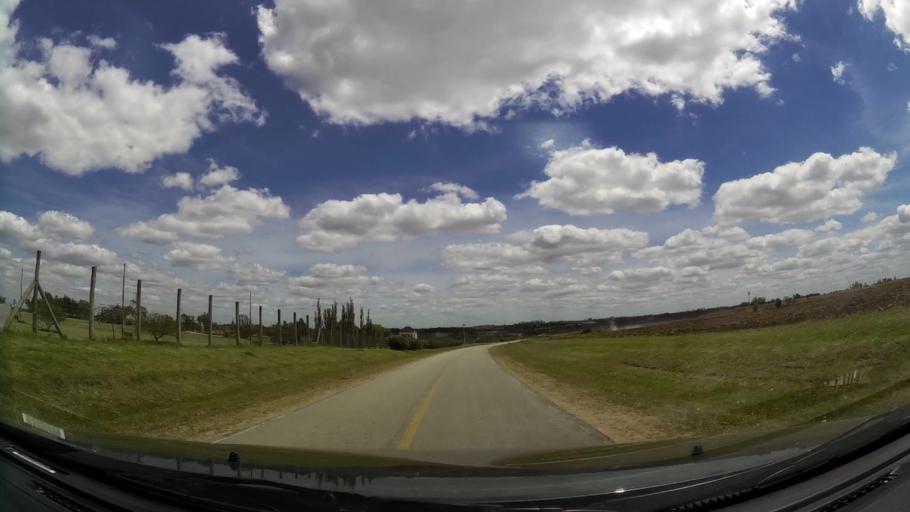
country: UY
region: Canelones
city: Colonia Nicolich
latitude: -34.7927
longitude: -56.0149
